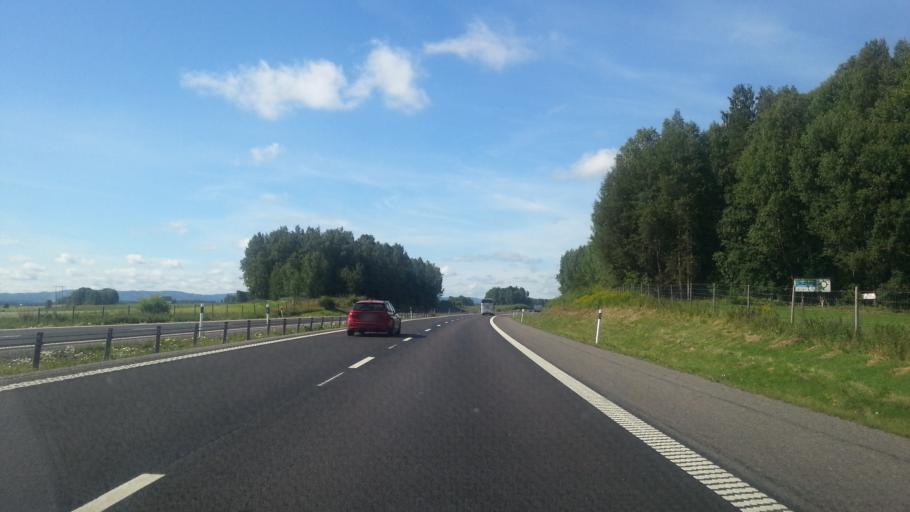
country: SE
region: Dalarna
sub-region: Borlange Kommun
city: Ornas
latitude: 60.4971
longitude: 15.5100
